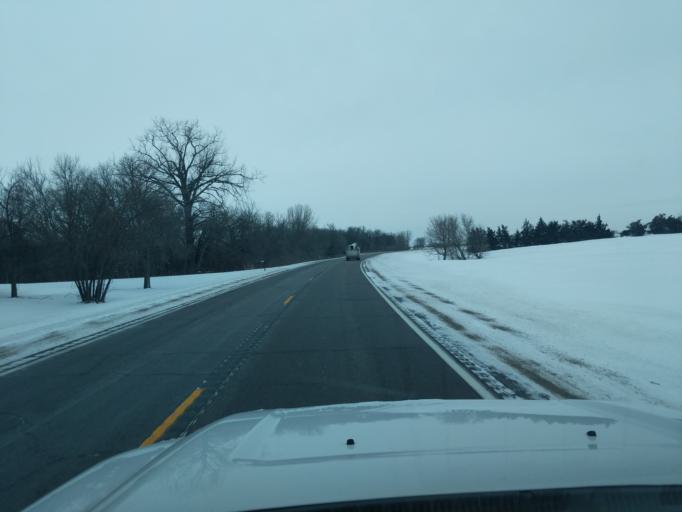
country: US
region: Minnesota
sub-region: Redwood County
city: Redwood Falls
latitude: 44.5685
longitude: -94.9948
